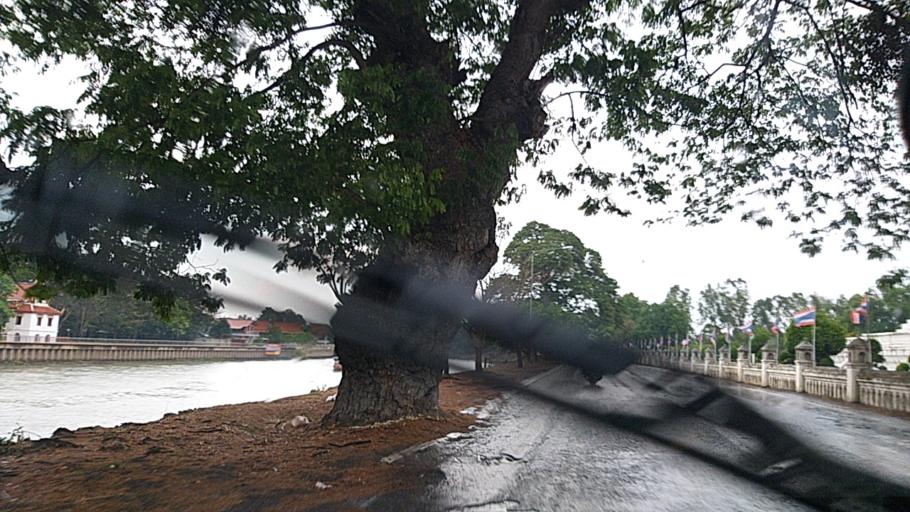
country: TH
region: Phra Nakhon Si Ayutthaya
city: Phra Nakhon Si Ayutthaya
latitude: 14.3523
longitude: 100.5471
